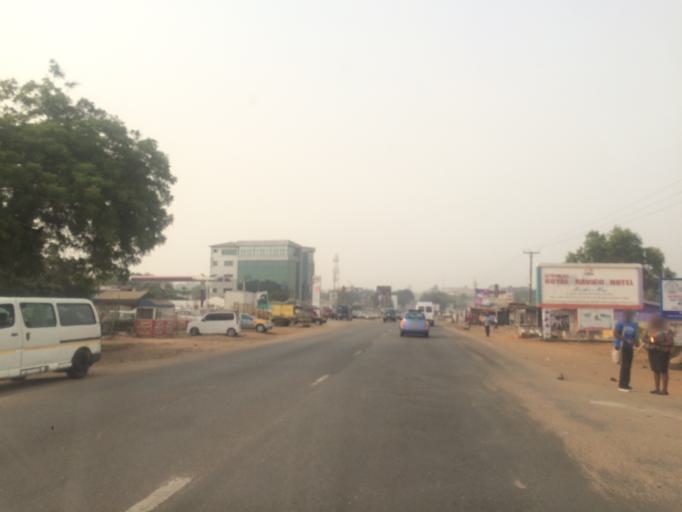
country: GH
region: Greater Accra
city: Nungua
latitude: 5.6106
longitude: -0.0755
